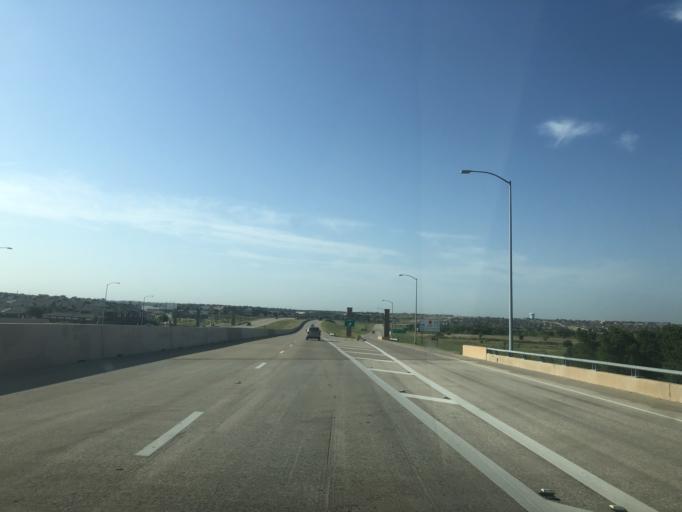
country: US
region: Texas
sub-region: Tarrant County
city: Benbrook
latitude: 32.6341
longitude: -97.4149
